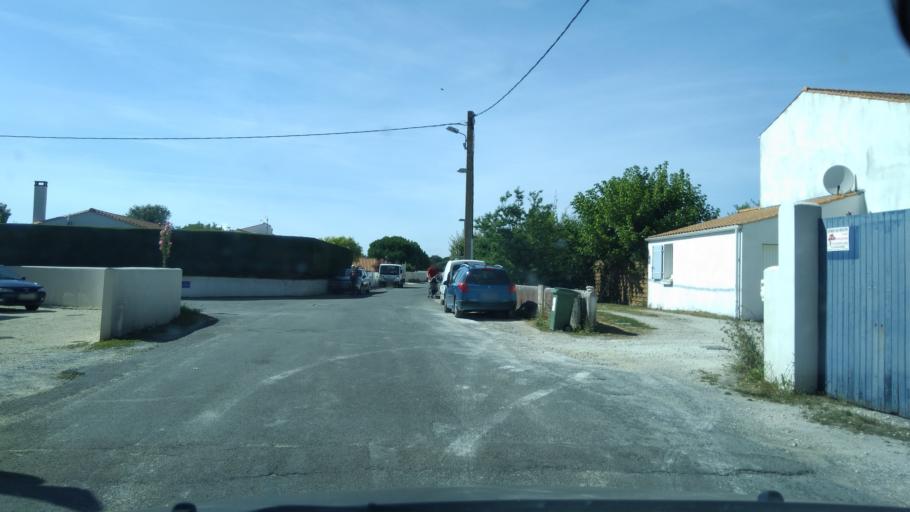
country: FR
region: Poitou-Charentes
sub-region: Departement de la Charente-Maritime
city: Dolus-d'Oleron
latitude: 45.9199
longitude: -1.3302
